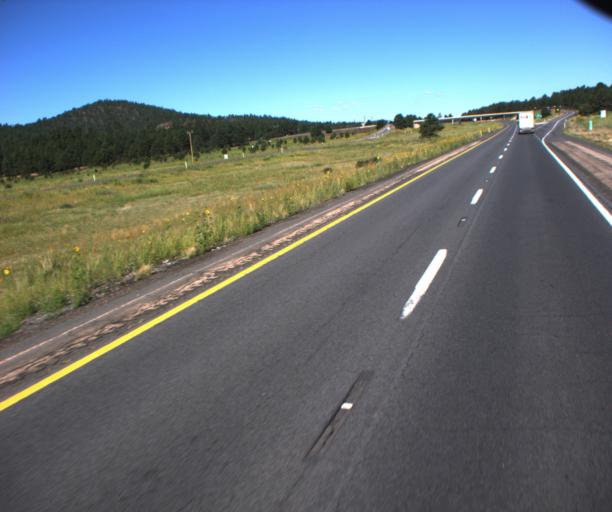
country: US
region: Arizona
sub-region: Coconino County
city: Parks
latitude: 35.2635
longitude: -112.0437
